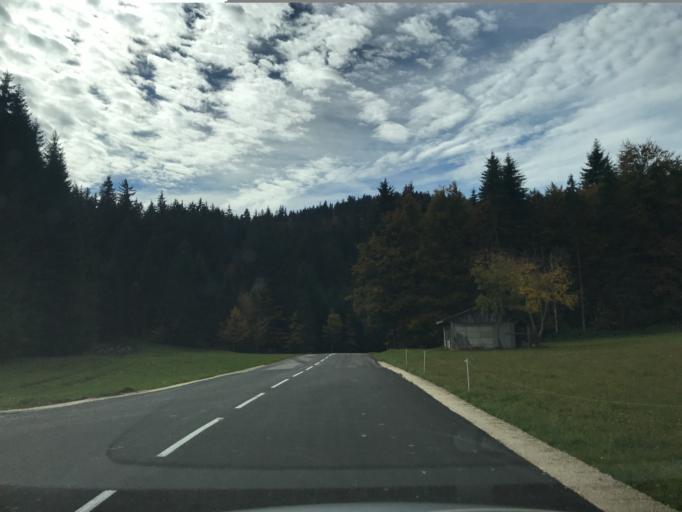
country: FR
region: Rhone-Alpes
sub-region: Departement de la Savoie
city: Vimines
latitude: 45.4546
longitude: 5.8588
